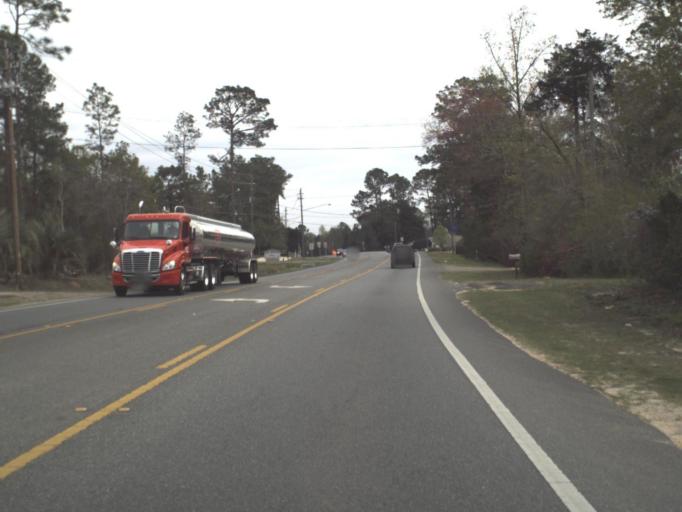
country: US
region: Florida
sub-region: Holmes County
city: Bonifay
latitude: 30.7751
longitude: -85.6828
